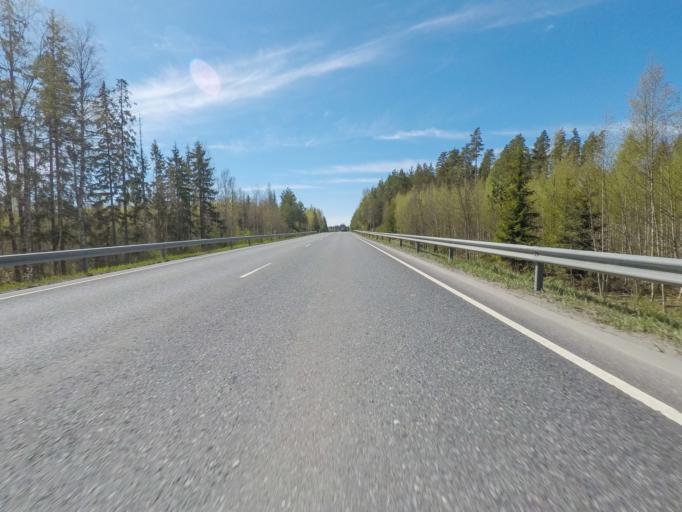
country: FI
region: Haeme
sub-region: Forssa
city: Humppila
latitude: 60.9687
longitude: 23.3983
